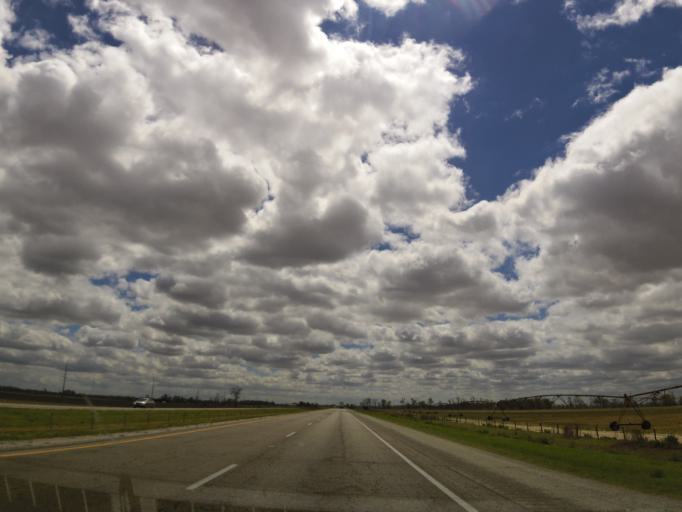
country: US
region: Arkansas
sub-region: Poinsett County
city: Trumann
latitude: 35.5851
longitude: -90.4970
